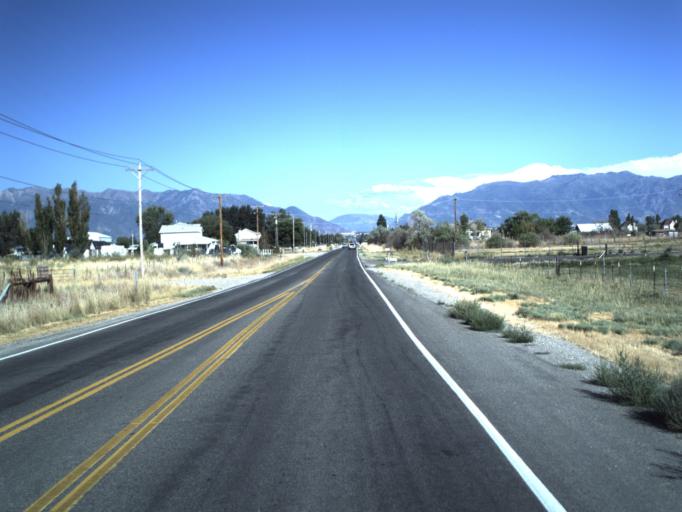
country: US
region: Utah
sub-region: Weber County
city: Hooper
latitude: 41.1398
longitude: -112.1072
